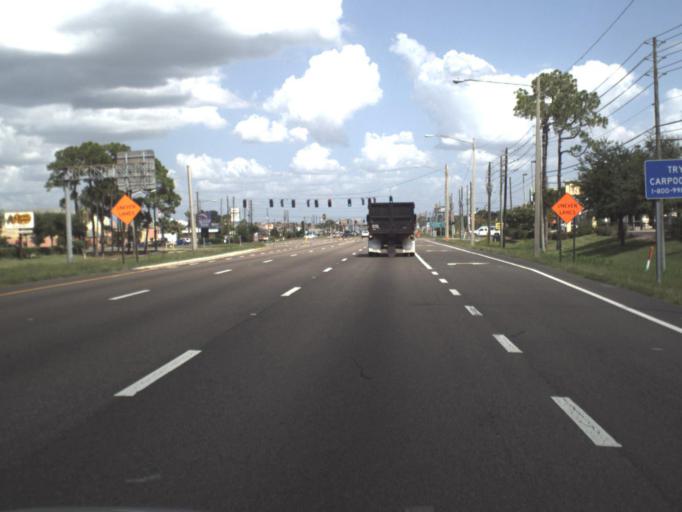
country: US
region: Florida
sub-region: Pinellas County
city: South Highpoint
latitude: 27.8938
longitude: -82.6899
